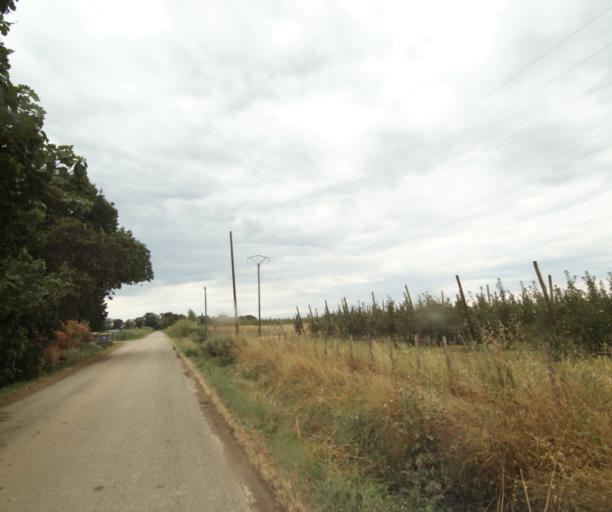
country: FR
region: Languedoc-Roussillon
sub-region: Departement de l'Herault
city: Marsillargues
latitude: 43.6246
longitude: 4.1656
